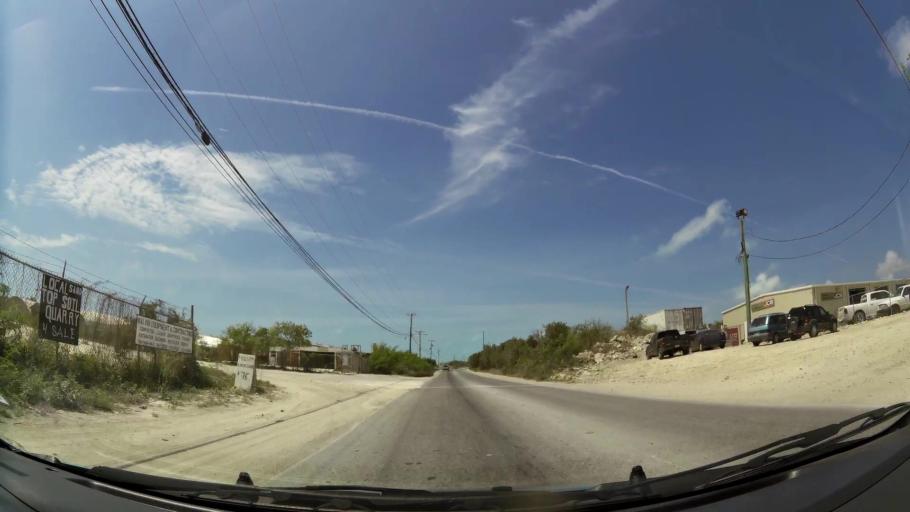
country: BS
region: Mayaguana
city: Abraham's Bay
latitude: 21.7703
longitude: -72.2594
